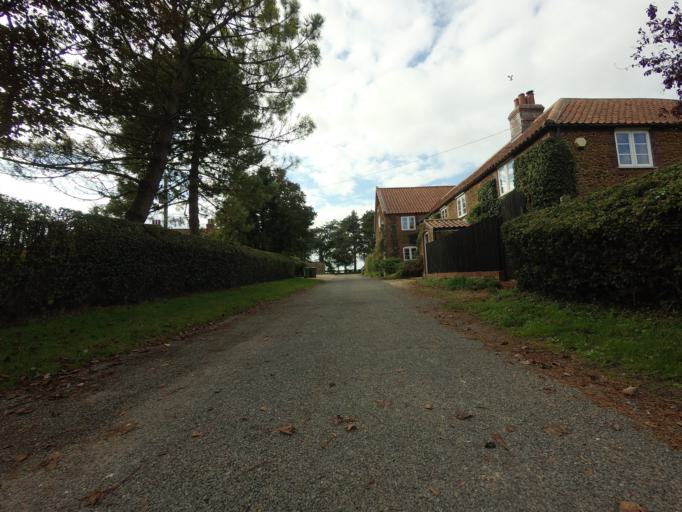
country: GB
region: England
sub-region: Norfolk
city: Dersingham
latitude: 52.8542
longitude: 0.5173
